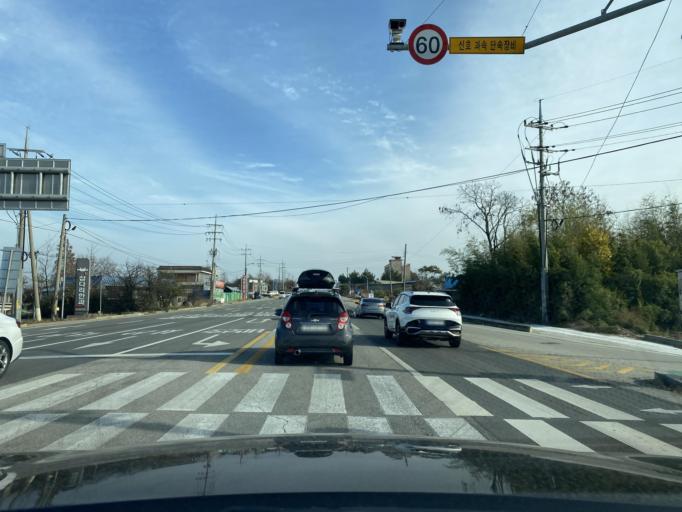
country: KR
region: Chungcheongnam-do
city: Yesan
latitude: 36.6906
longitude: 126.7429
